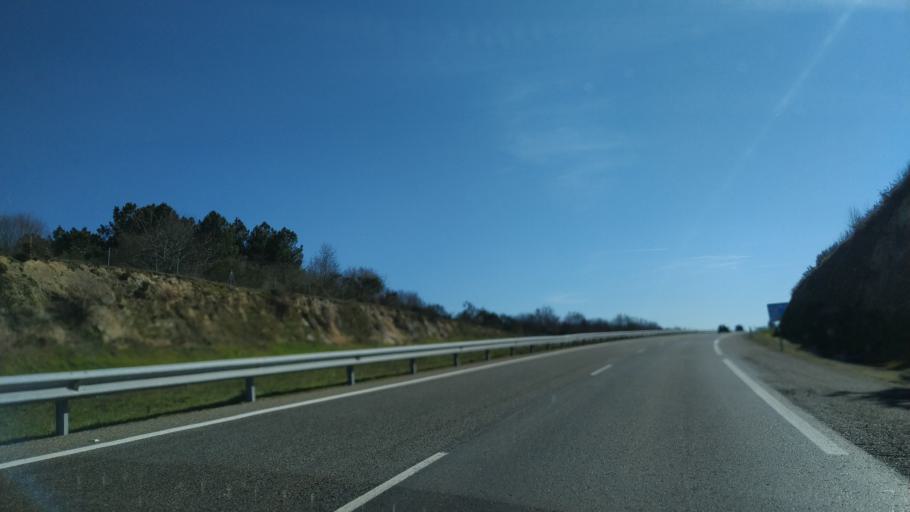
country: ES
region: Galicia
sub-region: Provincia de Ourense
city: Taboadela
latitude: 42.2138
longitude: -7.8372
